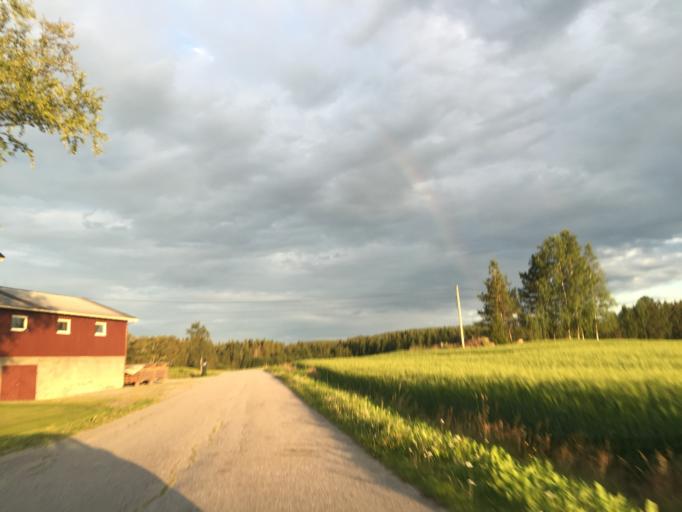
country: NO
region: Akershus
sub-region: Nes
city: Fjellfoten
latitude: 60.0914
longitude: 11.4861
